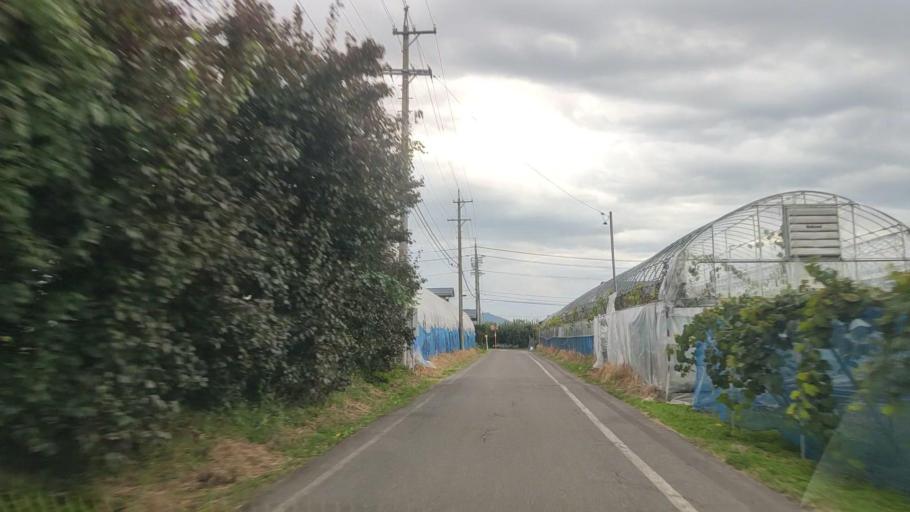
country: JP
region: Nagano
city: Nakano
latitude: 36.7636
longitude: 138.3862
